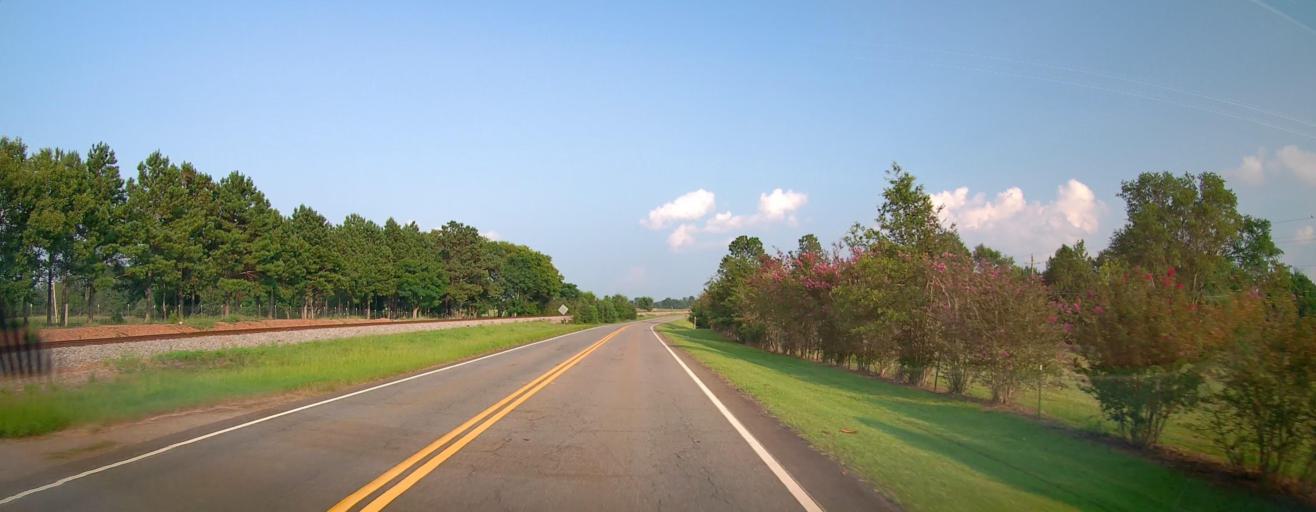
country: US
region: Georgia
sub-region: Jones County
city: Gray
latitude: 33.0415
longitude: -83.5490
